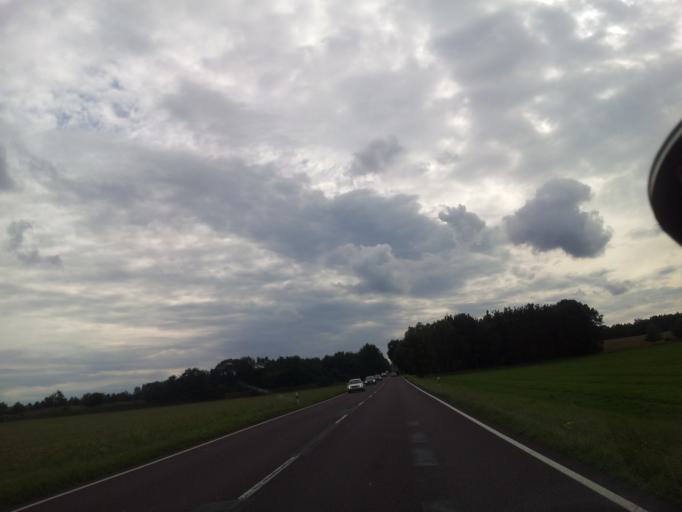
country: DE
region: Saxony-Anhalt
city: Burgstall
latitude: 52.4035
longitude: 11.6253
